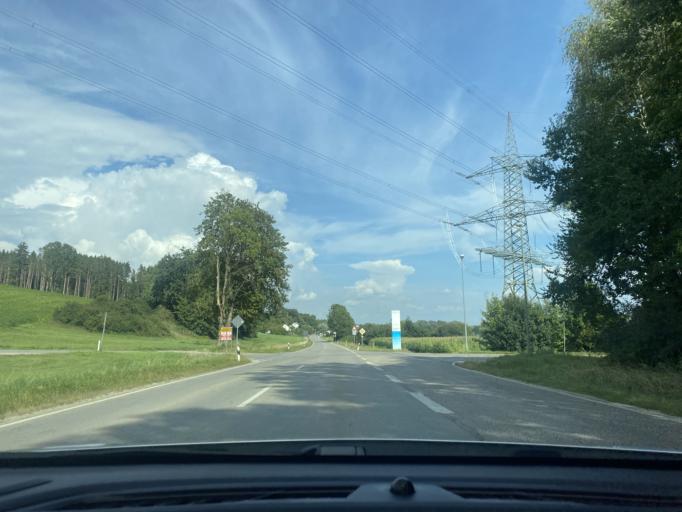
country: DE
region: Bavaria
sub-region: Upper Bavaria
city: Haag an der Amper
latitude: 48.4574
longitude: 11.8058
